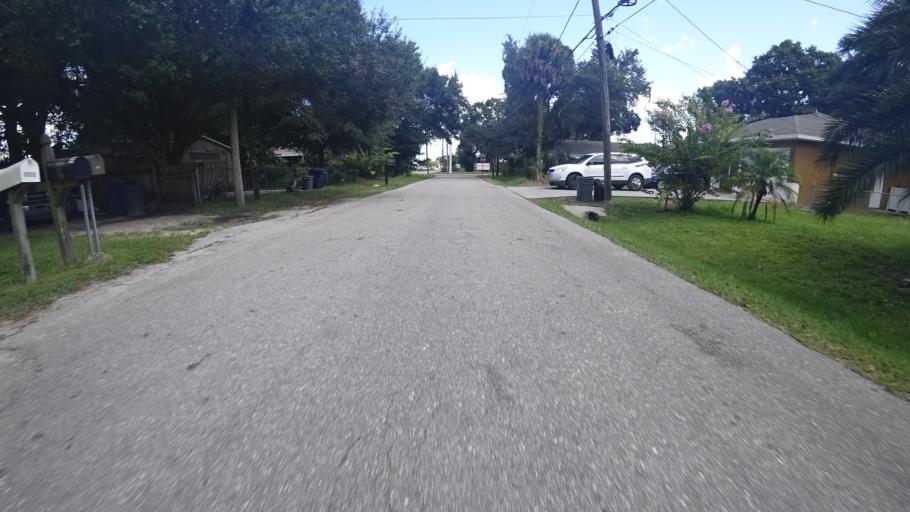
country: US
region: Florida
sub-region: Manatee County
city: West Samoset
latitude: 27.4727
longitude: -82.5502
